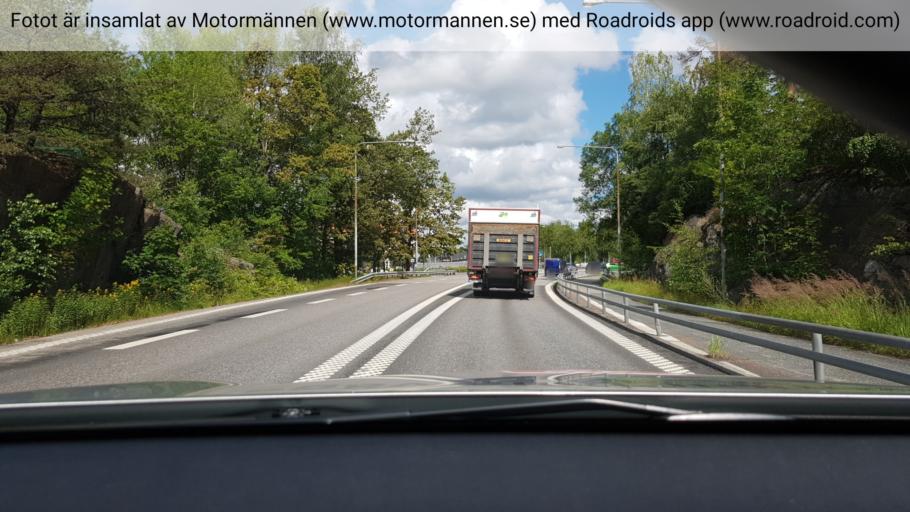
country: SE
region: Stockholm
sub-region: Tyreso Kommun
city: Bollmora
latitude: 59.2219
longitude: 18.2023
